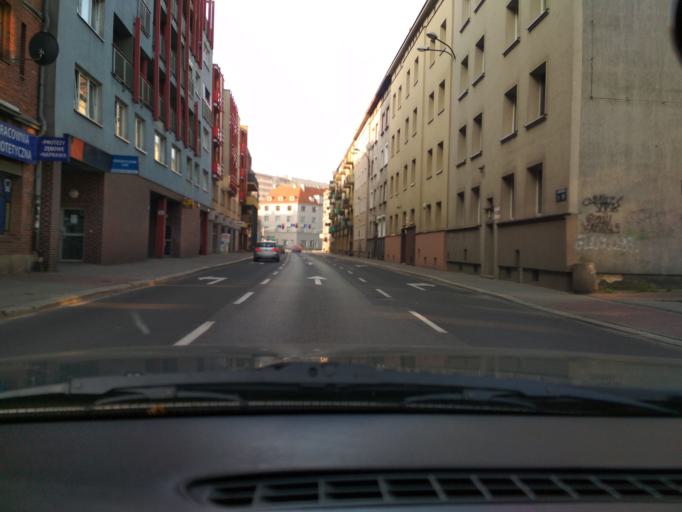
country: PL
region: Silesian Voivodeship
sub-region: Gliwice
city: Gliwice
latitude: 50.2912
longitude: 18.6681
